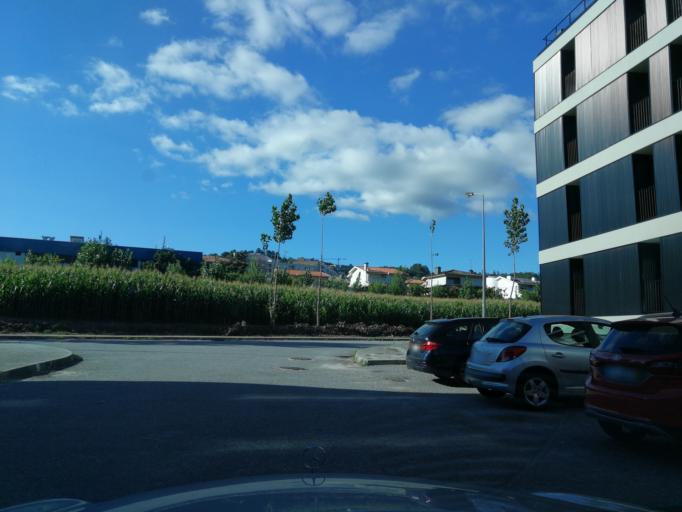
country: PT
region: Braga
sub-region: Braga
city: Adaufe
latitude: 41.5650
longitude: -8.3846
